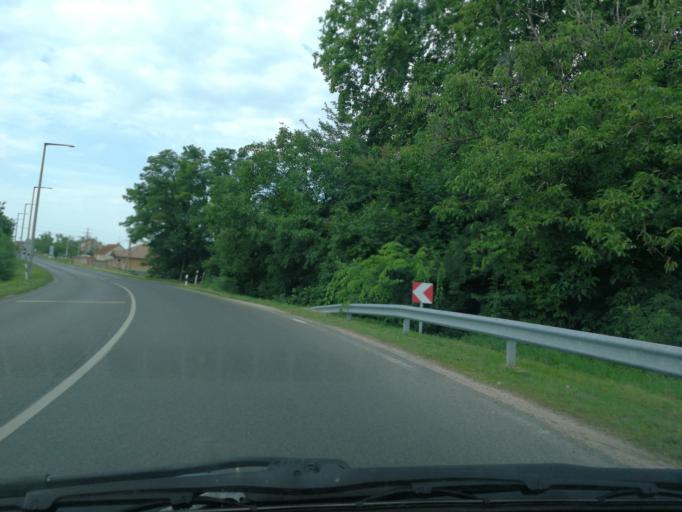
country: HU
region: Bacs-Kiskun
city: Baja
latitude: 46.2150
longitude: 18.9609
